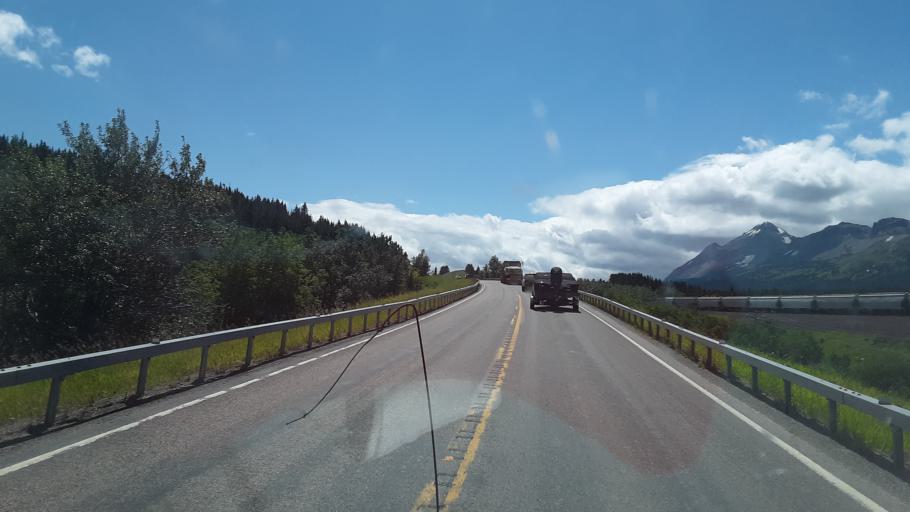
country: US
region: Montana
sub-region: Glacier County
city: South Browning
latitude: 48.3845
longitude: -113.2688
